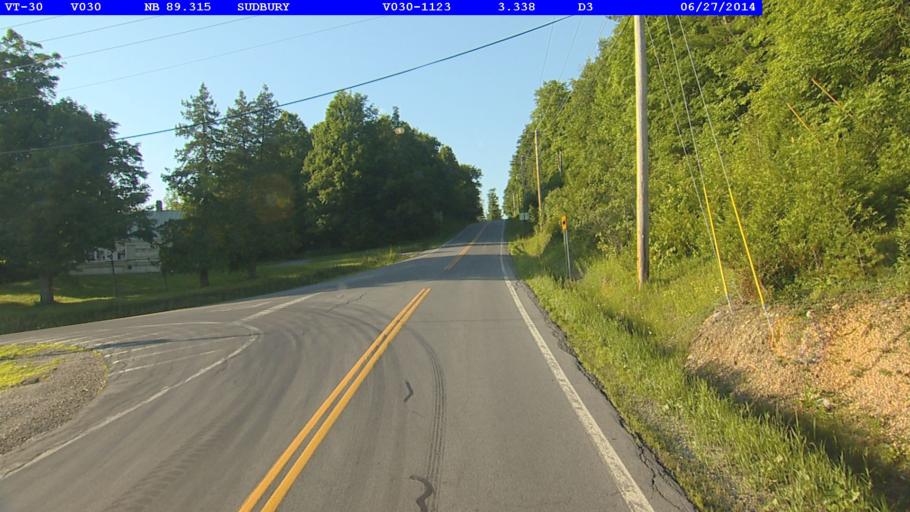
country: US
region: Vermont
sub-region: Rutland County
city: Brandon
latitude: 43.7960
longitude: -73.2056
